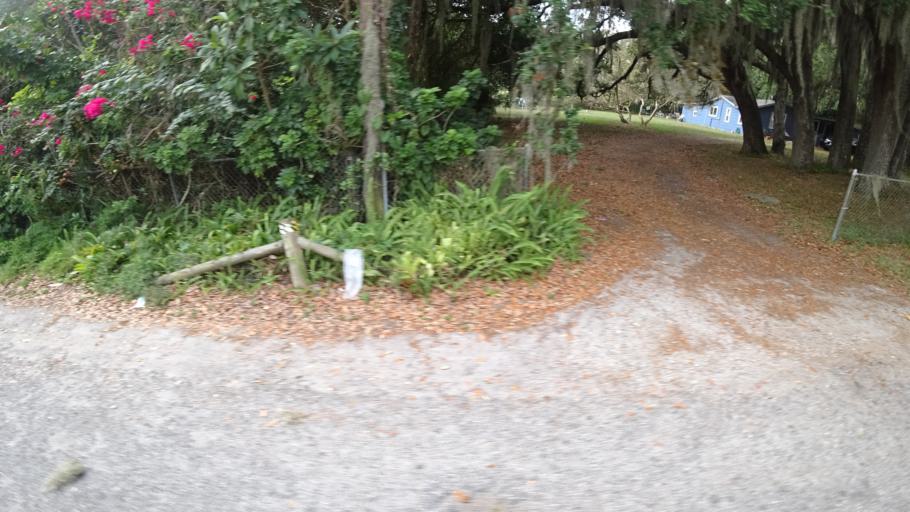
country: US
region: Florida
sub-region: Sarasota County
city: North Sarasota
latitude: 27.4059
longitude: -82.5107
